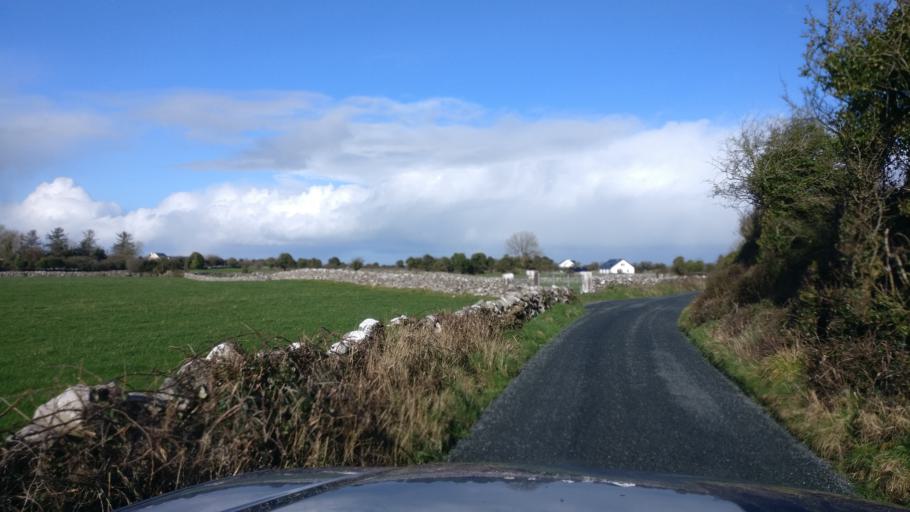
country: IE
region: Connaught
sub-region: County Galway
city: Athenry
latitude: 53.2356
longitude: -8.7734
